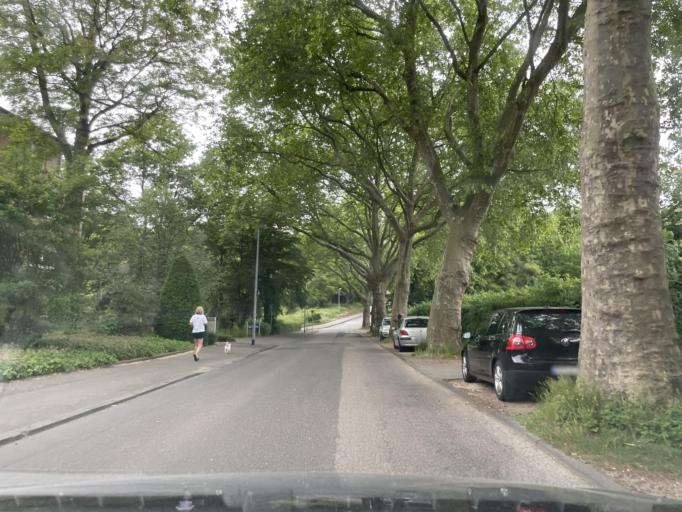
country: DE
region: North Rhine-Westphalia
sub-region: Regierungsbezirk Dusseldorf
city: Monchengladbach
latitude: 51.1365
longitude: 6.4567
